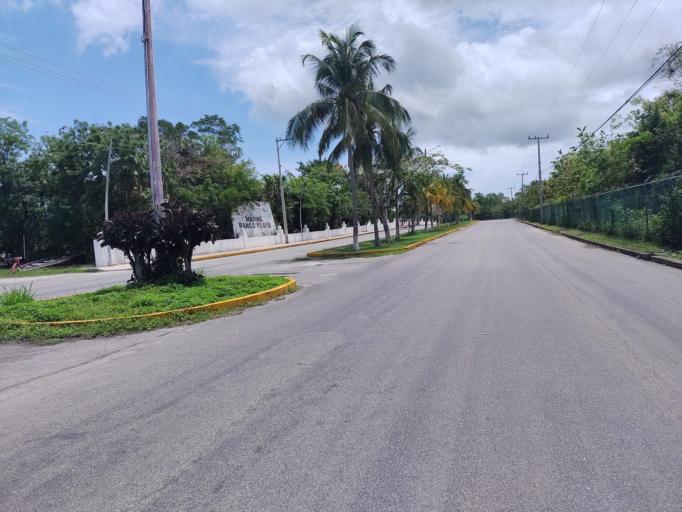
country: MX
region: Quintana Roo
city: San Miguel de Cozumel
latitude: 20.5262
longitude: -86.9402
